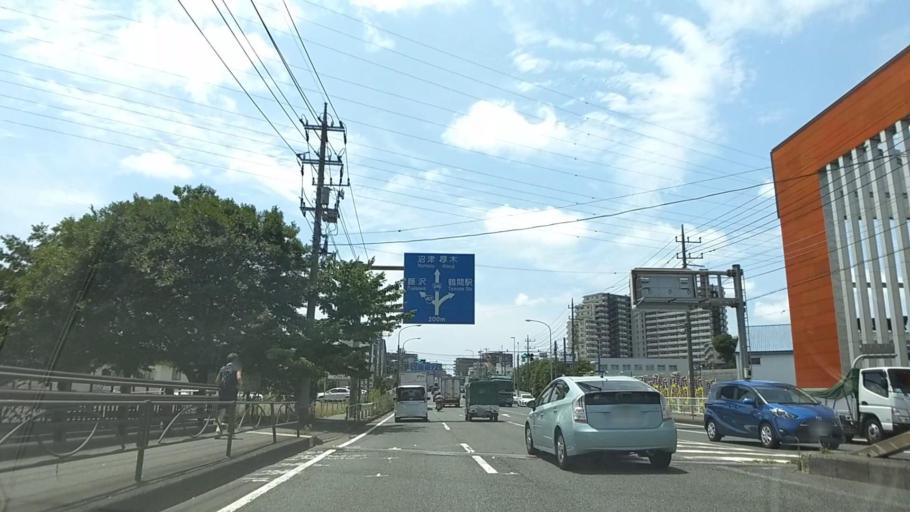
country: JP
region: Kanagawa
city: Minami-rinkan
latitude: 35.4960
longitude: 139.4656
